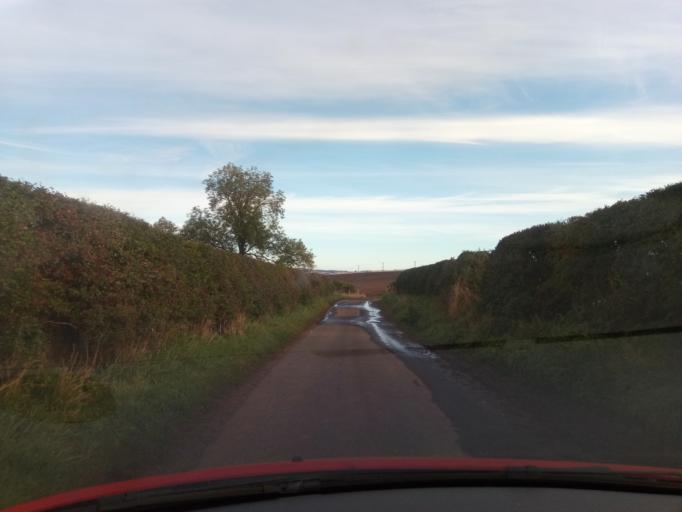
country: GB
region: Scotland
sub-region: The Scottish Borders
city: Kelso
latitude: 55.5075
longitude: -2.4201
